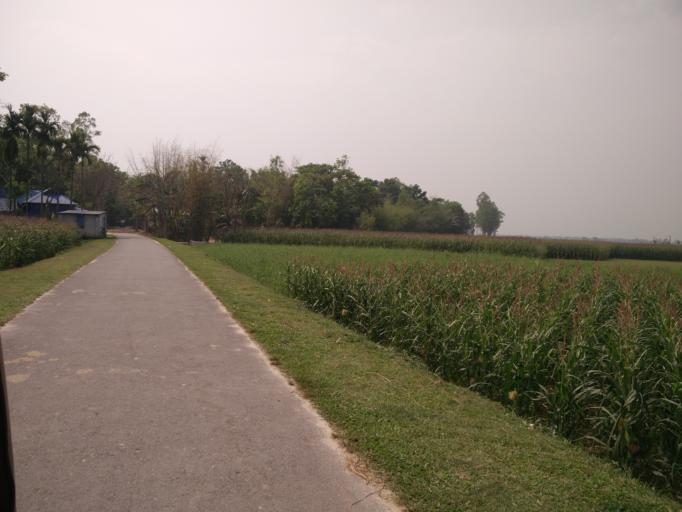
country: BD
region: Dhaka
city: Muktagacha
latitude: 24.9007
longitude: 90.2591
